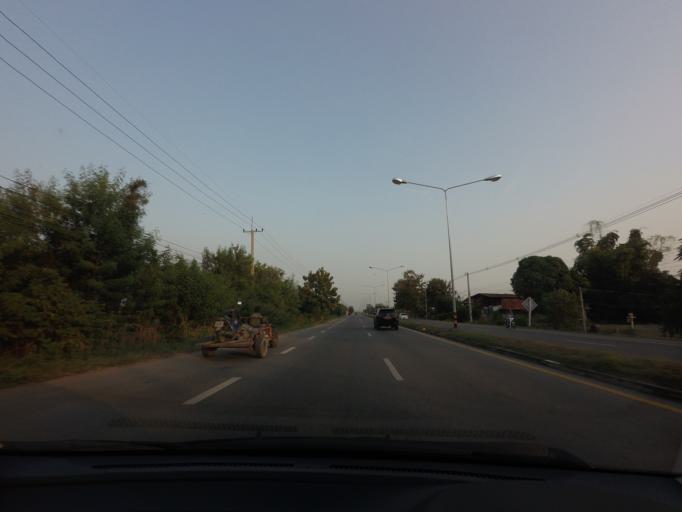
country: TH
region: Sukhothai
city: Kong Krailat
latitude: 17.0126
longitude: 99.9176
